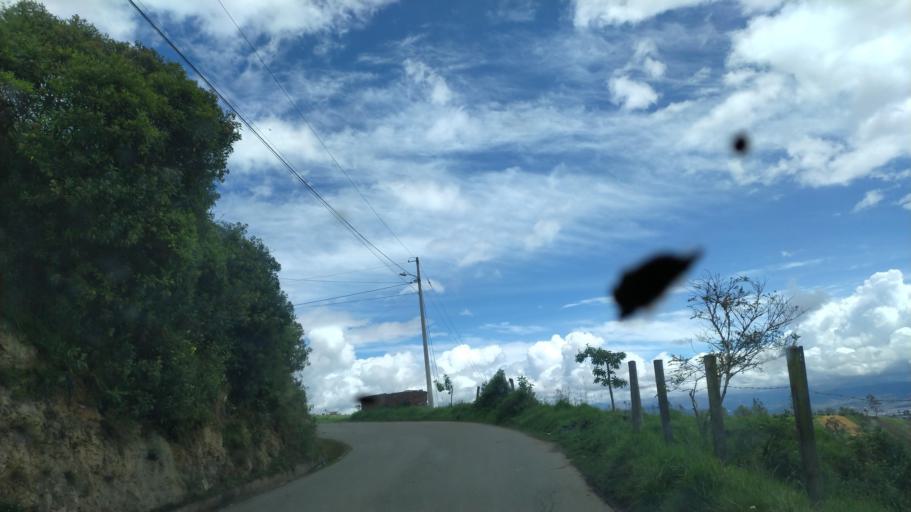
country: EC
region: Chimborazo
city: Riobamba
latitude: -1.6855
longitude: -78.5760
